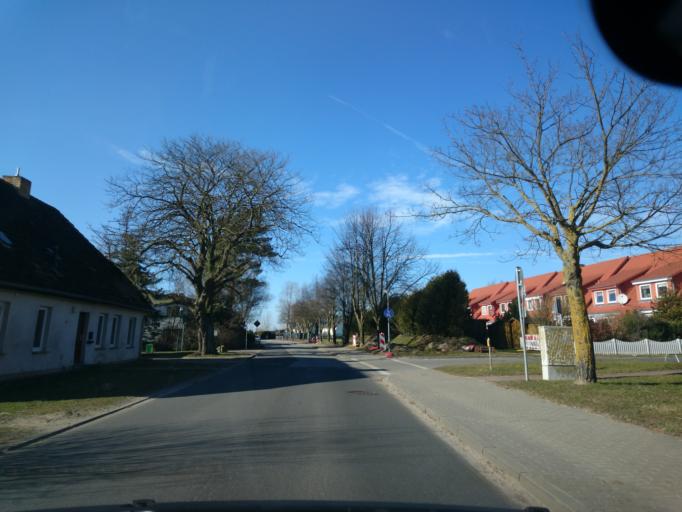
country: DE
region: Mecklenburg-Vorpommern
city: Borgerende-Rethwisch
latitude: 54.1414
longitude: 11.9337
